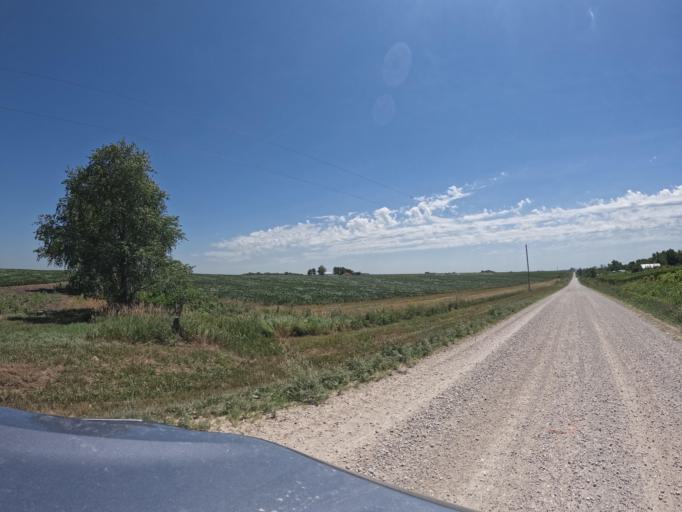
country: US
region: Iowa
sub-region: Keokuk County
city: Sigourney
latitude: 41.4126
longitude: -92.3164
